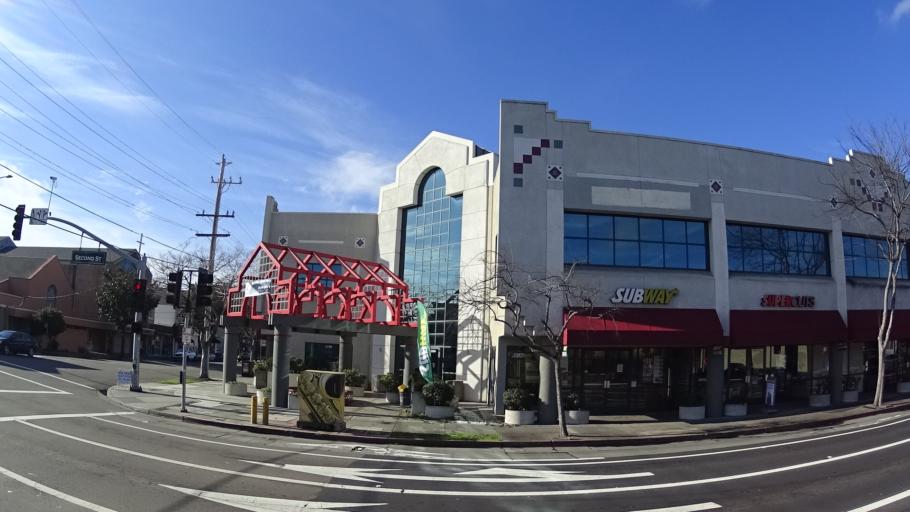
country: US
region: California
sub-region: Alameda County
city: Hayward
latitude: 37.6754
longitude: -122.0795
